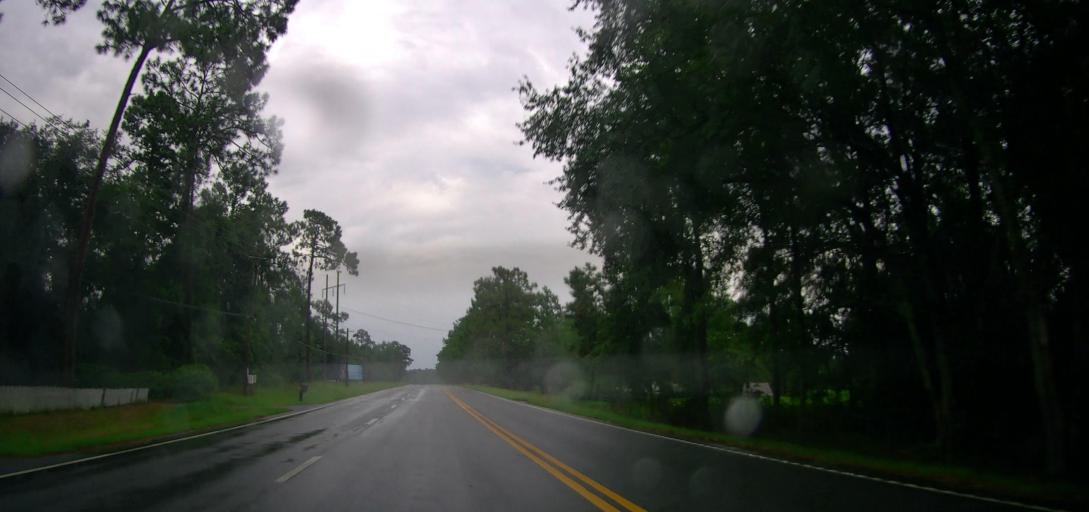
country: US
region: Georgia
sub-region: Ware County
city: Deenwood
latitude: 31.2613
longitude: -82.3858
